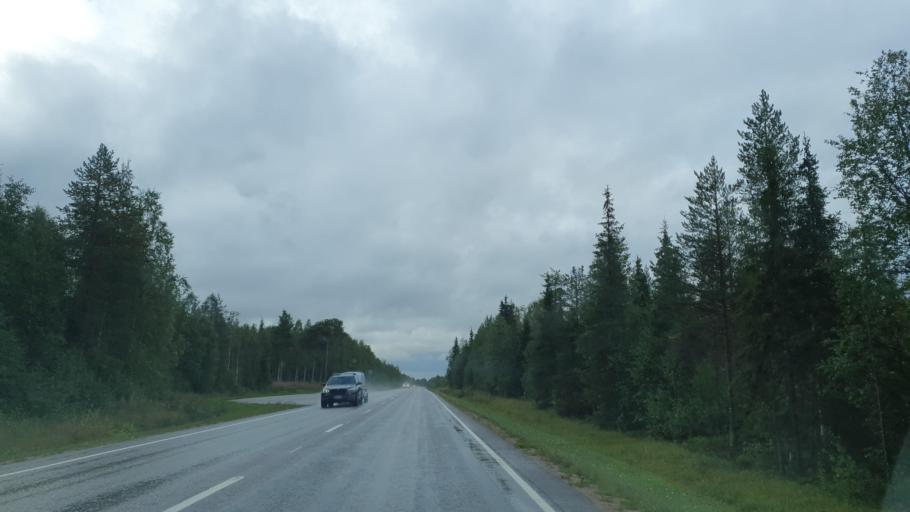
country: FI
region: Lapland
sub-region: Tunturi-Lappi
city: Kolari
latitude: 67.2414
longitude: 23.8807
